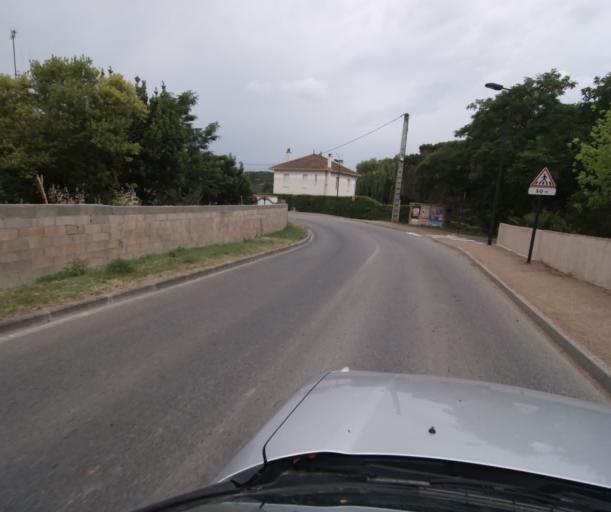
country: FR
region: Languedoc-Roussillon
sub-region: Departement de l'Aude
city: Limoux
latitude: 43.0650
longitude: 2.2242
